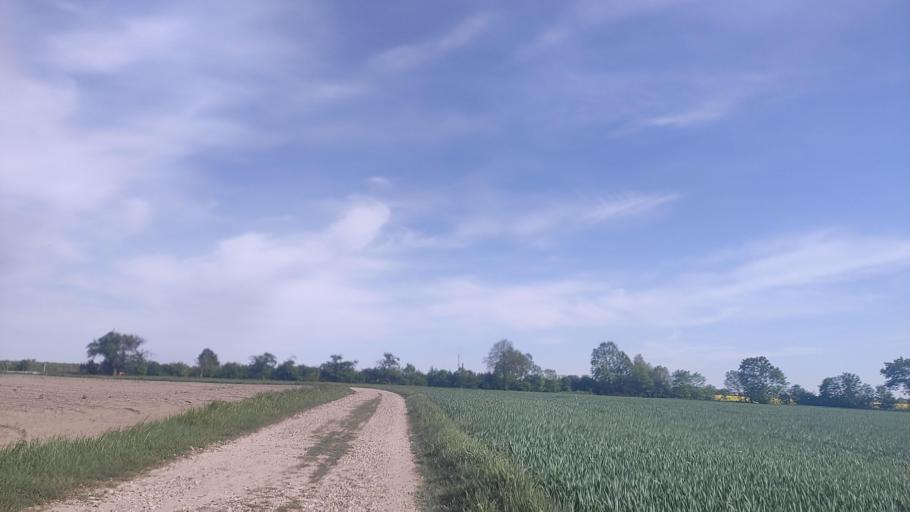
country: PL
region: Greater Poland Voivodeship
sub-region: Powiat poznanski
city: Swarzedz
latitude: 52.4138
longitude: 17.1525
